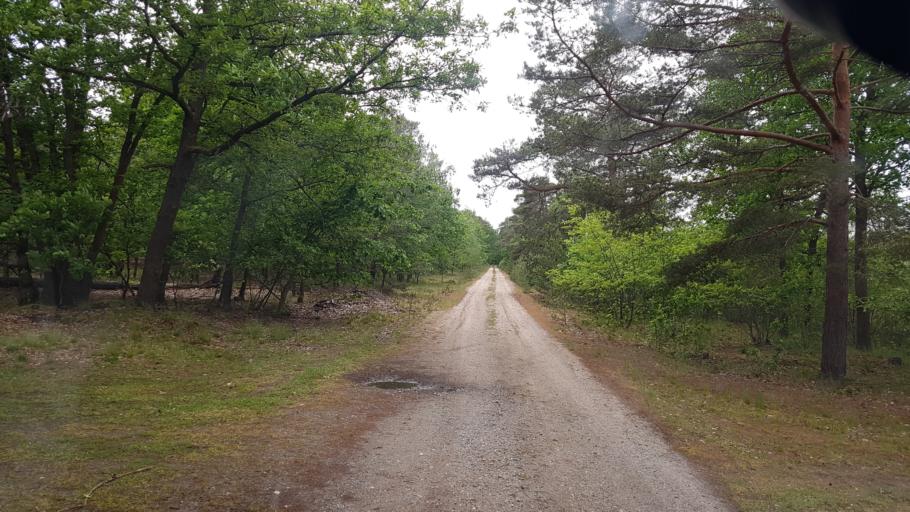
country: DE
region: Brandenburg
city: Hohenleipisch
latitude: 51.5247
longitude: 13.5380
